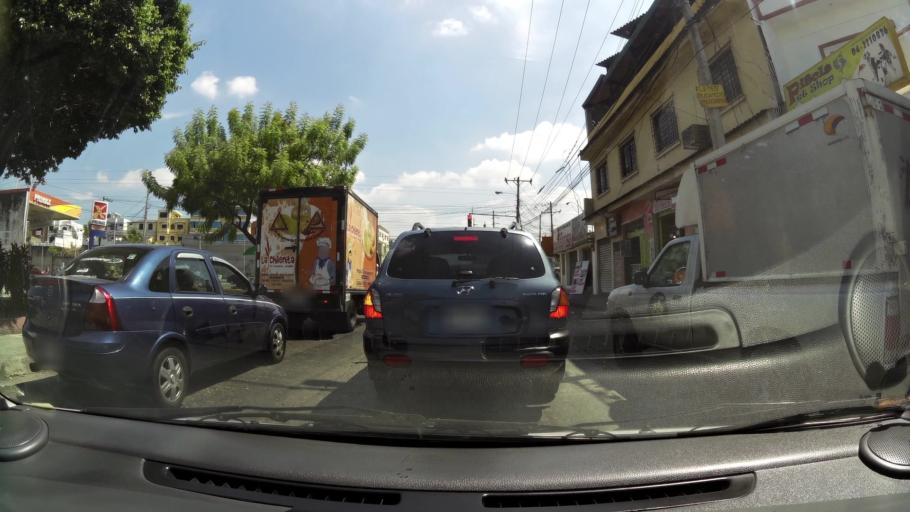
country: EC
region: Guayas
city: Eloy Alfaro
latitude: -2.1207
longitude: -79.9048
